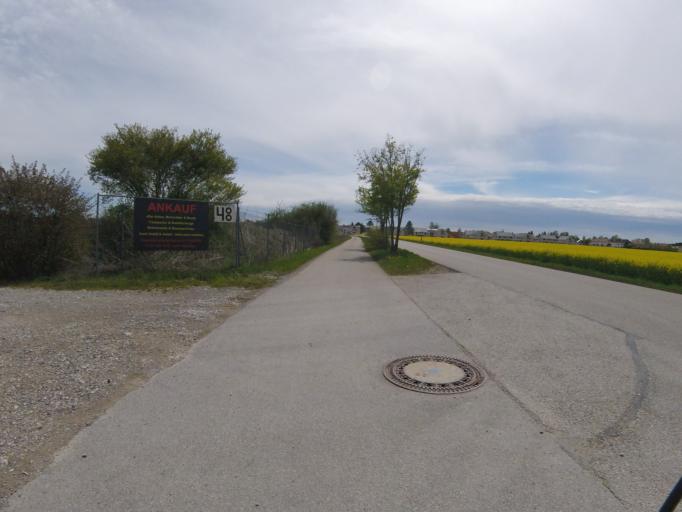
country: DE
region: Bavaria
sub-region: Upper Bavaria
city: Hohenkirchen-Siegertsbrunn
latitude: 48.0264
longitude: 11.7088
